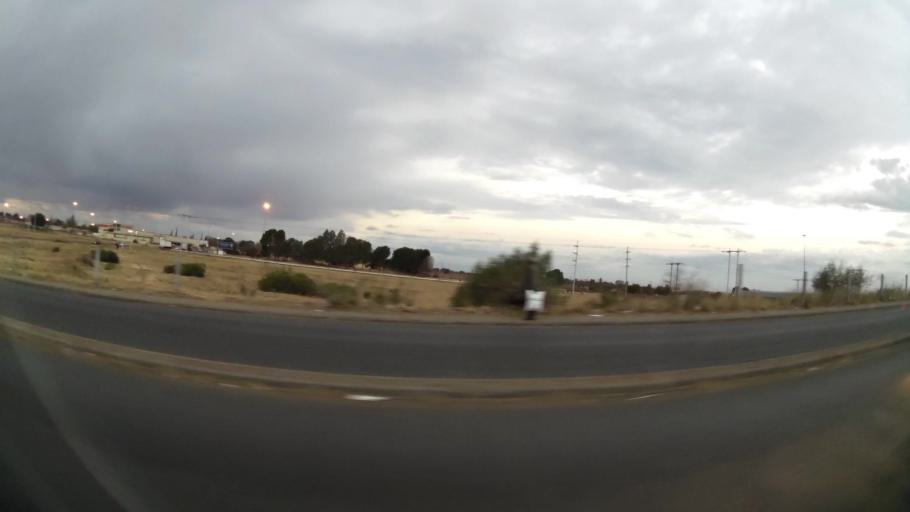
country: ZA
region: Orange Free State
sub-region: Lejweleputswa District Municipality
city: Welkom
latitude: -27.9761
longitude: 26.7743
